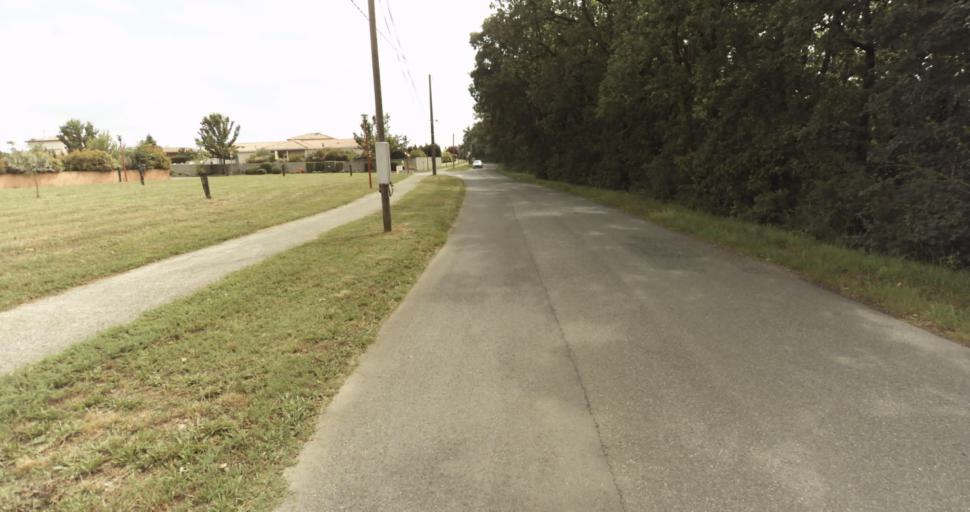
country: FR
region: Midi-Pyrenees
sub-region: Departement de la Haute-Garonne
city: Fontenilles
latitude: 43.5535
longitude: 1.2000
